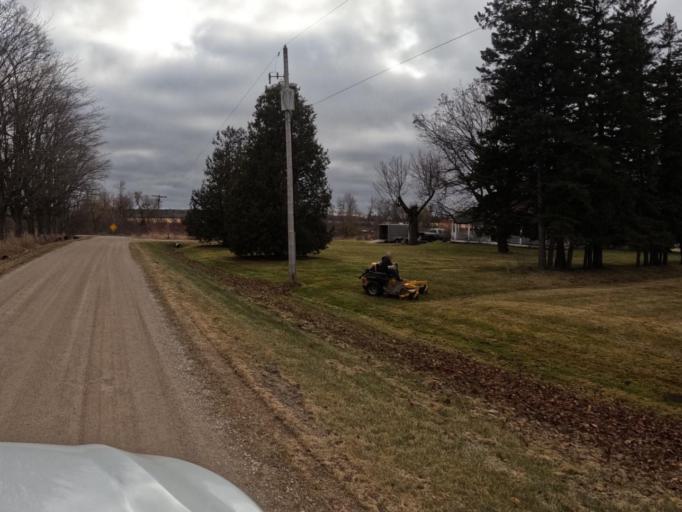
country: CA
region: Ontario
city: Shelburne
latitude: 43.8887
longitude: -80.3285
